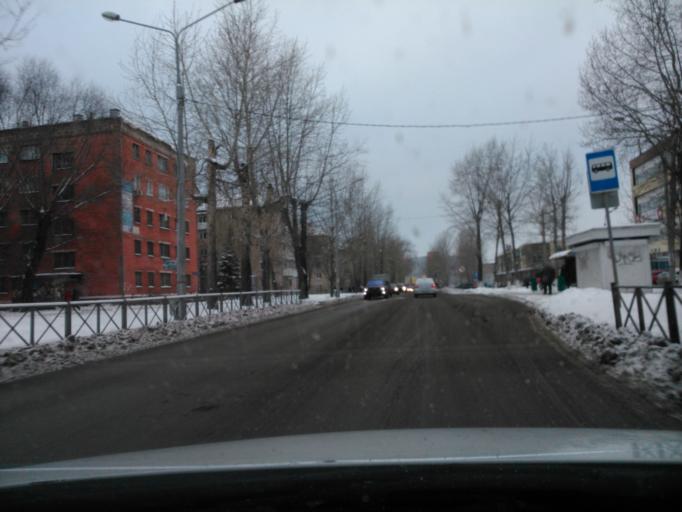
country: RU
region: Perm
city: Perm
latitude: 57.9879
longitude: 56.2059
